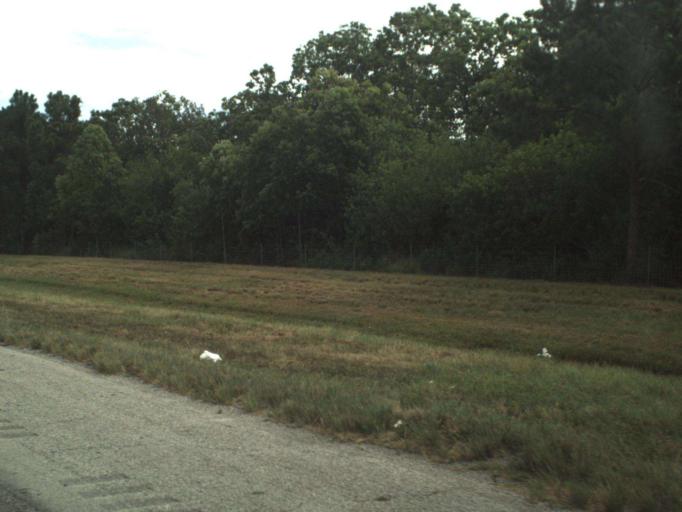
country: US
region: Florida
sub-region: Saint Lucie County
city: Port Saint Lucie
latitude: 27.1936
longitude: -80.3994
